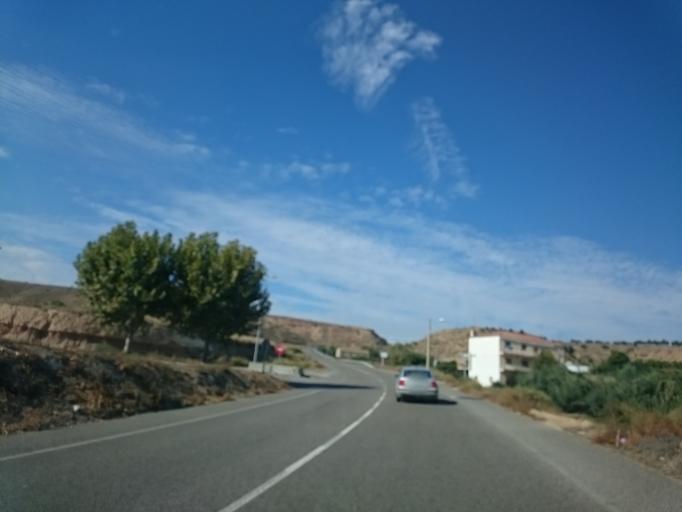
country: ES
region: Catalonia
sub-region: Provincia de Lleida
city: Alguaire
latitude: 41.7324
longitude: 0.5856
